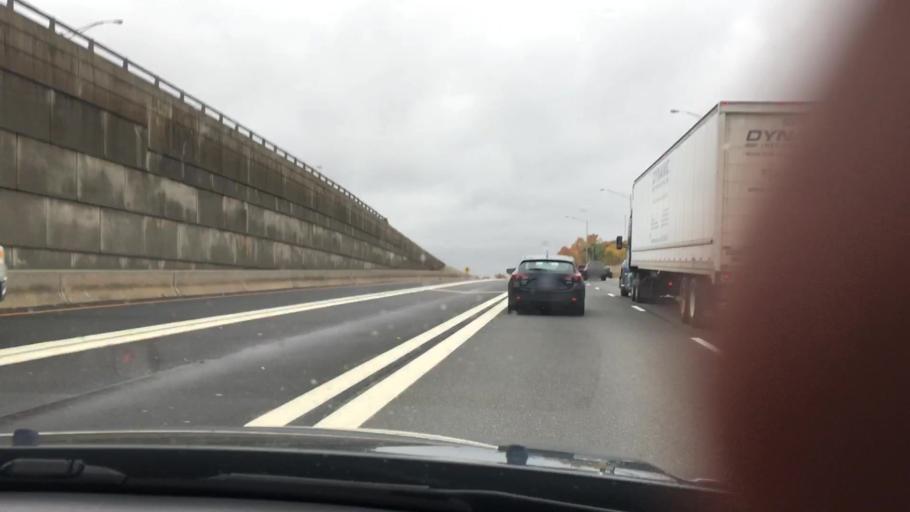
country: US
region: Connecticut
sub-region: Hartford County
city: East Hartford
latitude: 41.7747
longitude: -72.5860
